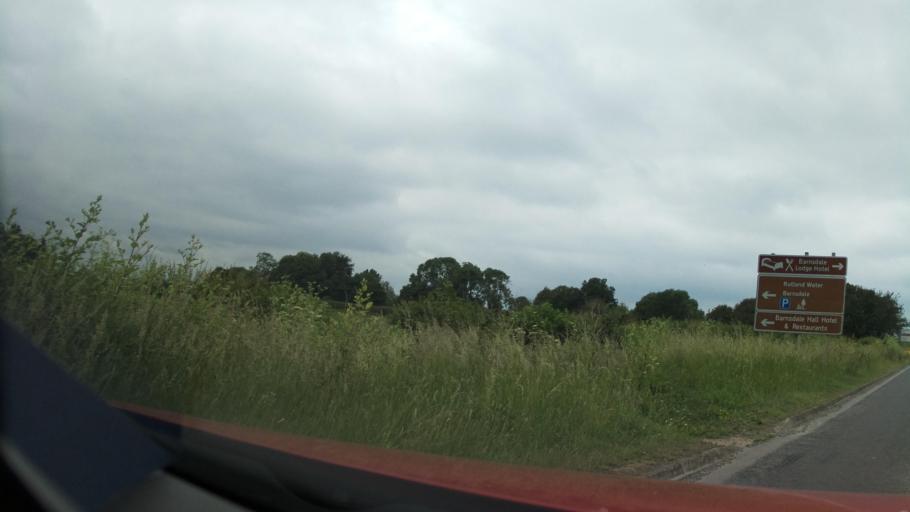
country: GB
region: England
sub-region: District of Rutland
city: Exton
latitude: 52.6736
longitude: -0.6572
